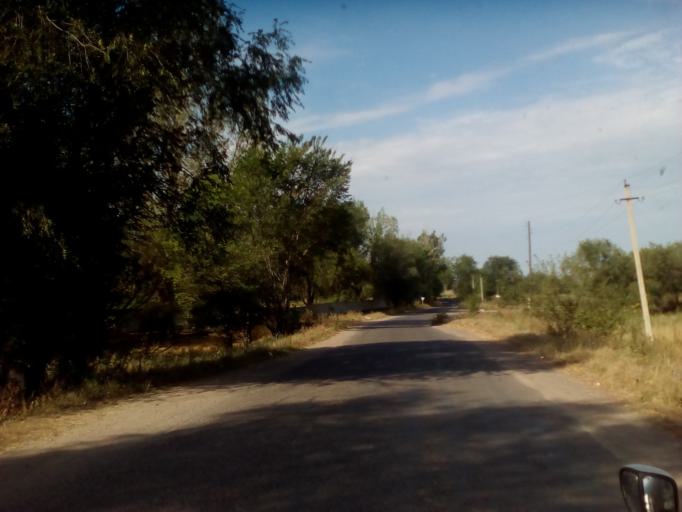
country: KZ
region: Almaty Oblysy
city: Burunday
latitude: 43.1643
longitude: 76.3859
